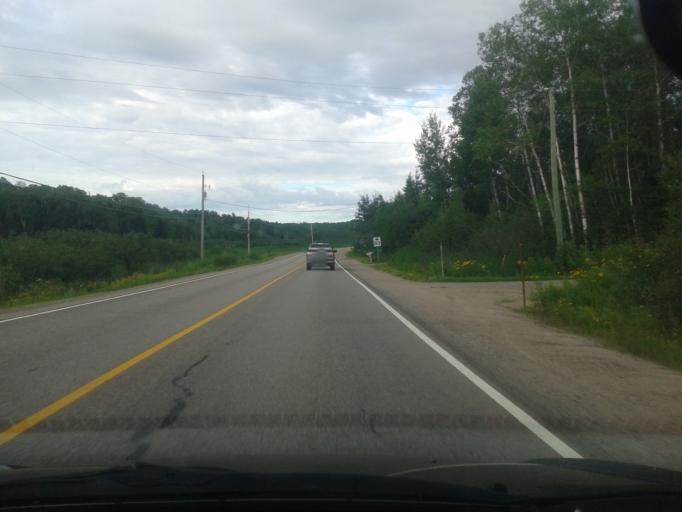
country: CA
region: Ontario
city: Powassan
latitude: 46.1894
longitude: -79.2992
